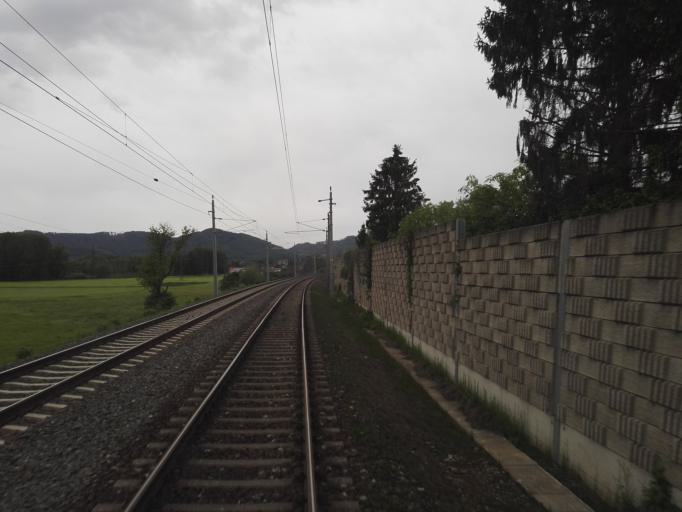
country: AT
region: Styria
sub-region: Politischer Bezirk Graz-Umgebung
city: Gratwein
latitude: 47.1402
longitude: 15.3238
